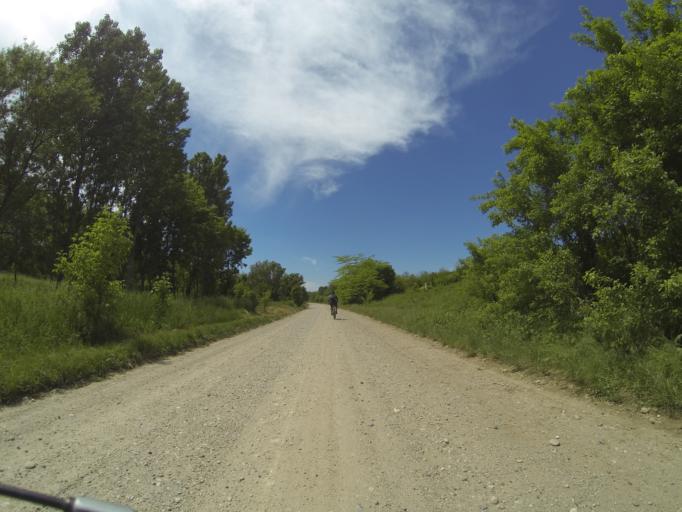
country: RO
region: Dolj
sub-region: Comuna Teslui
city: Teslui
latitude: 44.1989
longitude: 24.1239
